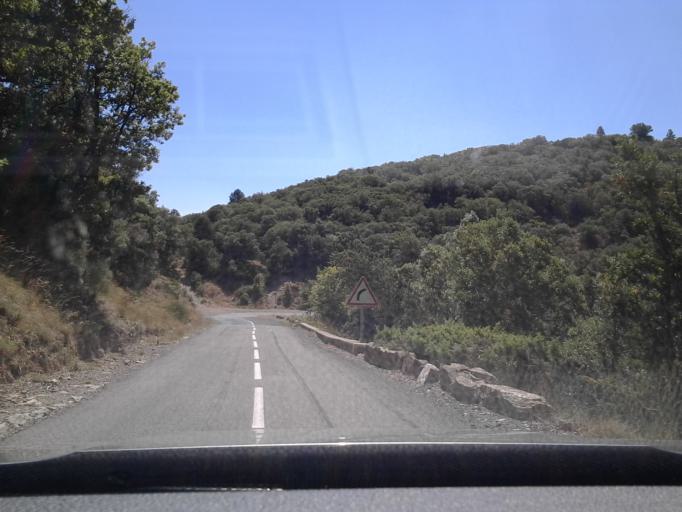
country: FR
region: Languedoc-Roussillon
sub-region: Departement de l'Herault
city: Montpeyroux
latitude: 43.7370
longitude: 3.4622
